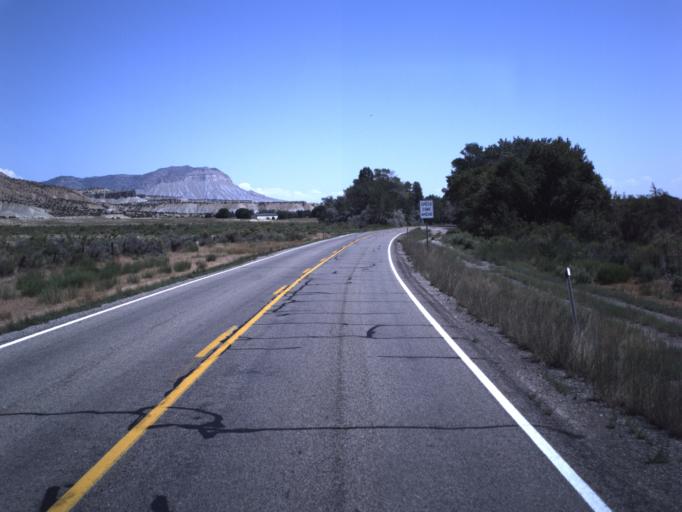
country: US
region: Utah
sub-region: Emery County
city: Ferron
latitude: 38.9175
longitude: -111.2632
